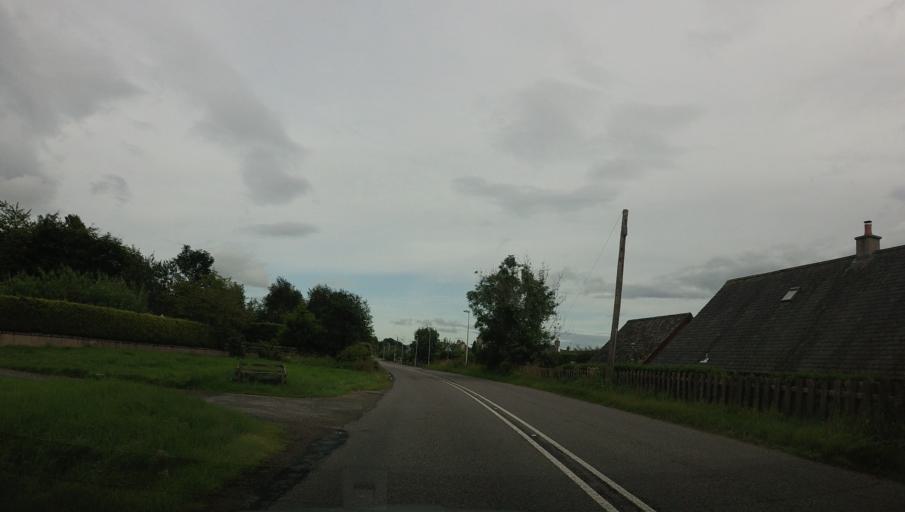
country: GB
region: Scotland
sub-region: Aberdeenshire
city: Banchory
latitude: 57.0615
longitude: -2.5617
